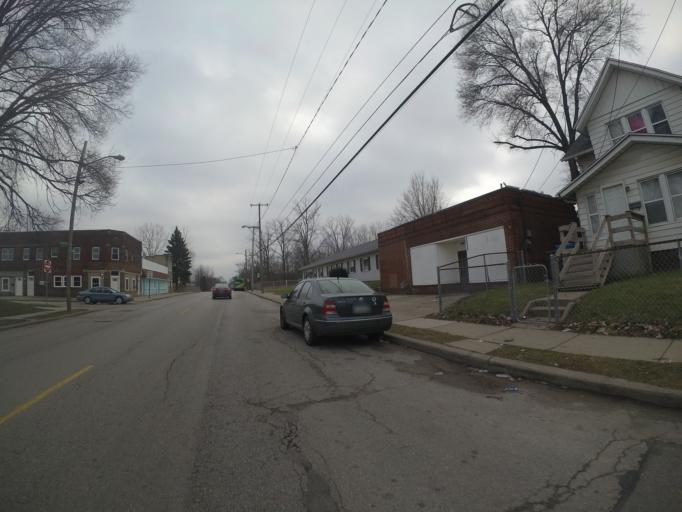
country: US
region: Ohio
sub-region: Lucas County
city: Oregon
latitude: 41.6273
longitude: -83.5154
